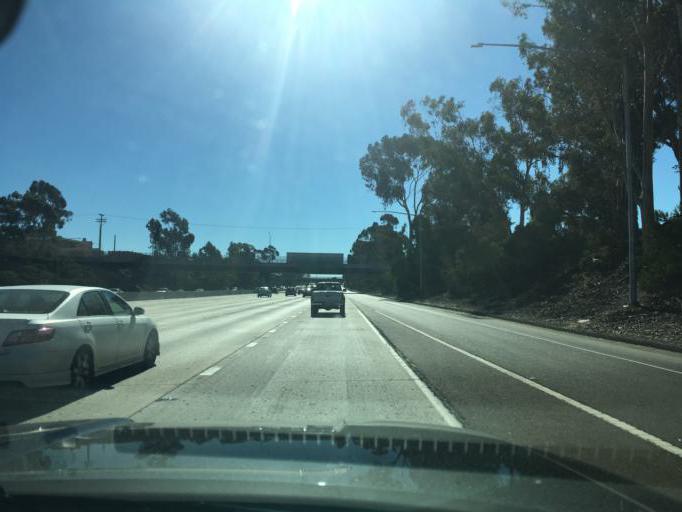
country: US
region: California
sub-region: San Diego County
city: National City
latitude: 32.7022
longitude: -117.0951
